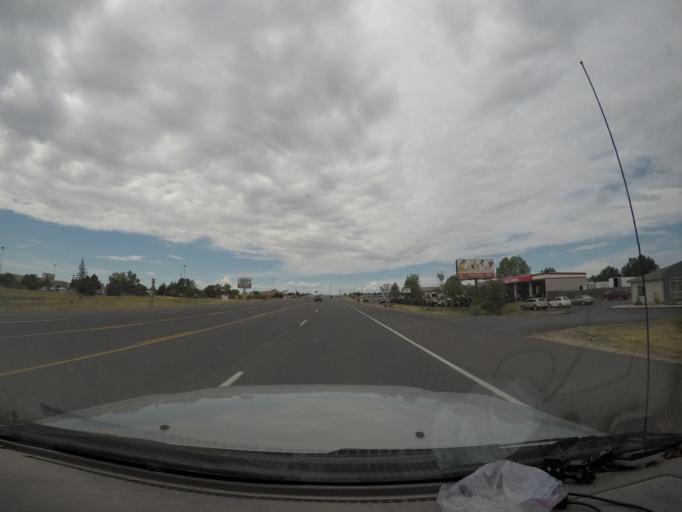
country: US
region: Wyoming
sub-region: Laramie County
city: Fox Farm-College
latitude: 41.1407
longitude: -104.7639
